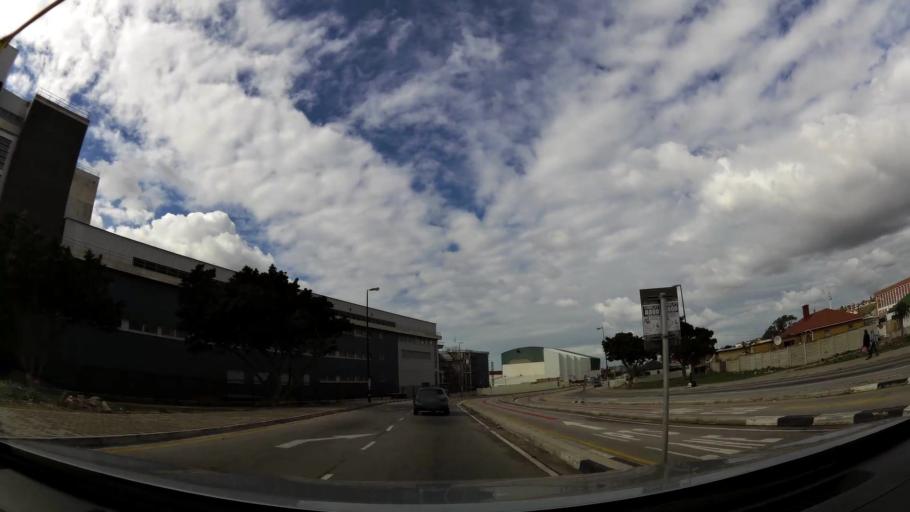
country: ZA
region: Eastern Cape
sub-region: Nelson Mandela Bay Metropolitan Municipality
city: Port Elizabeth
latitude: -33.9358
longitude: 25.5875
